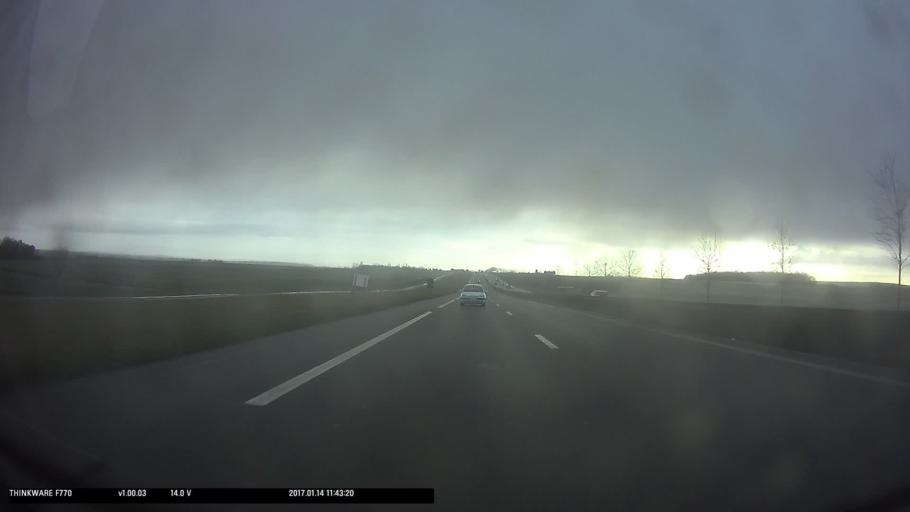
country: FR
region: Ile-de-France
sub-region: Departement du Val-d'Oise
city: Vigny
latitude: 49.0770
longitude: 1.9455
